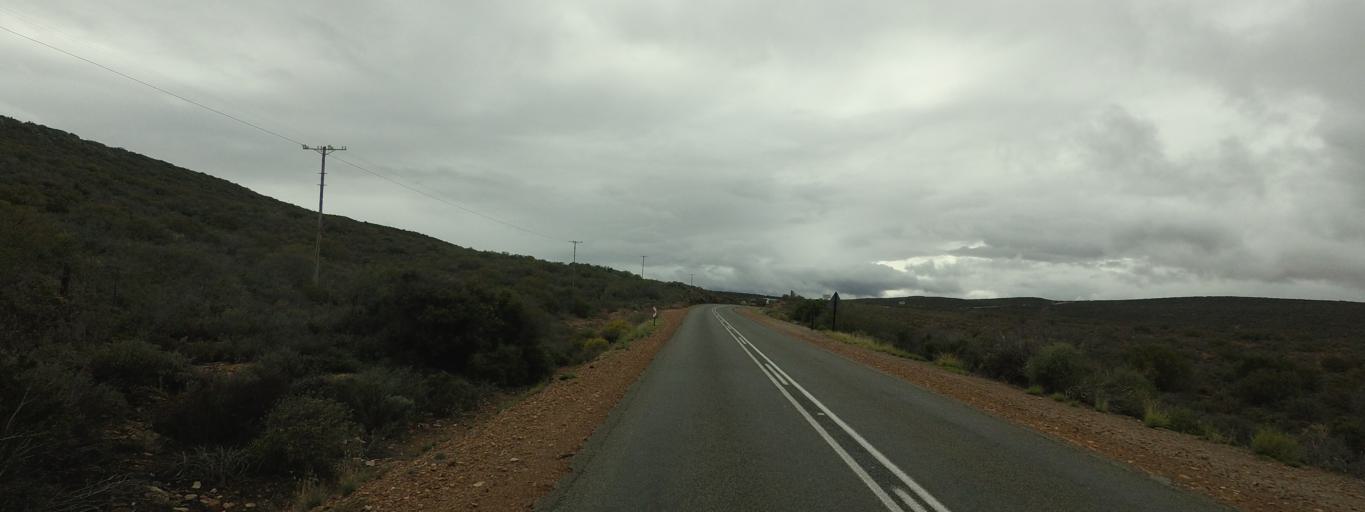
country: ZA
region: Western Cape
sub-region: Eden District Municipality
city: Oudtshoorn
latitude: -33.6916
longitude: 22.2722
